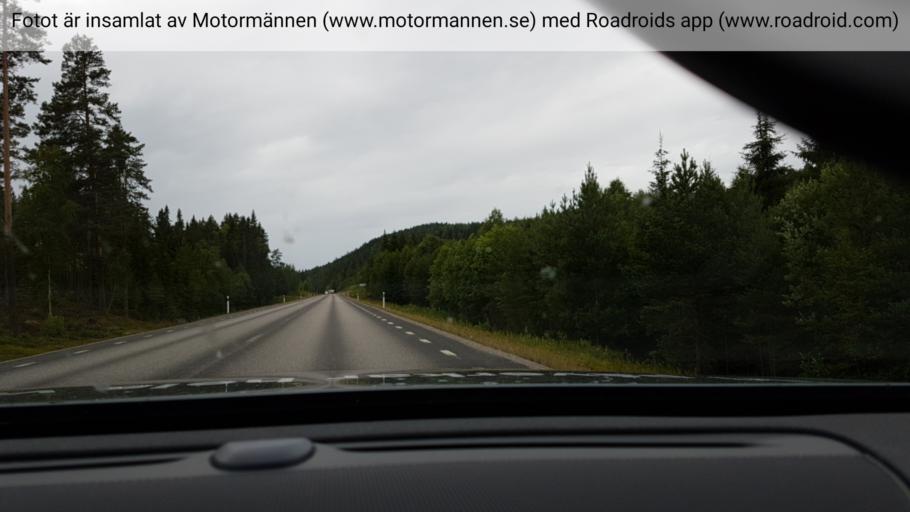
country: SE
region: Dalarna
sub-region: Faluns Kommun
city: Bjursas
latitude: 60.7525
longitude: 15.3474
